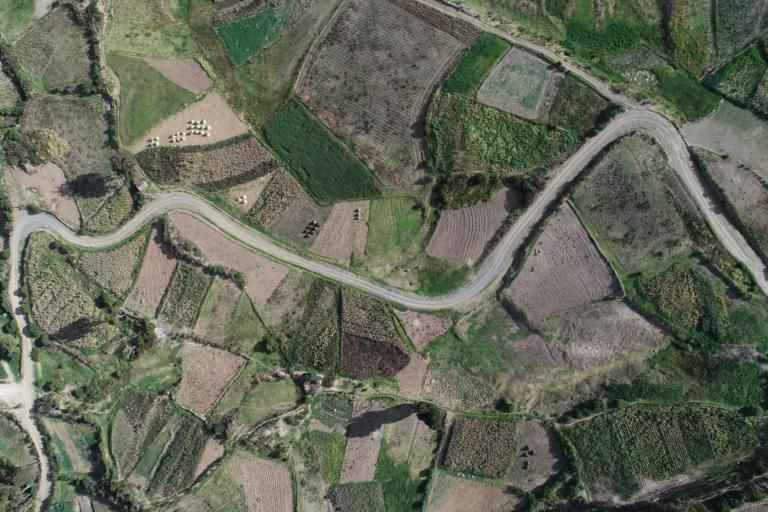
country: BO
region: La Paz
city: La Paz
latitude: -16.5535
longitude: -67.9897
